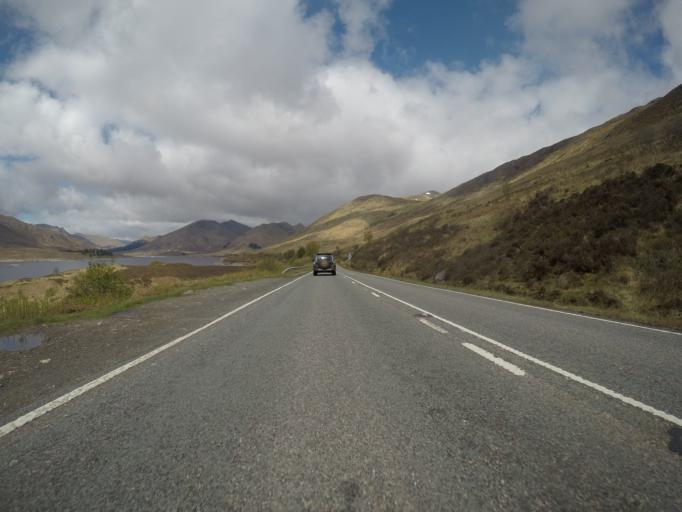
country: GB
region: Scotland
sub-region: Highland
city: Spean Bridge
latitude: 57.1493
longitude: -5.1198
